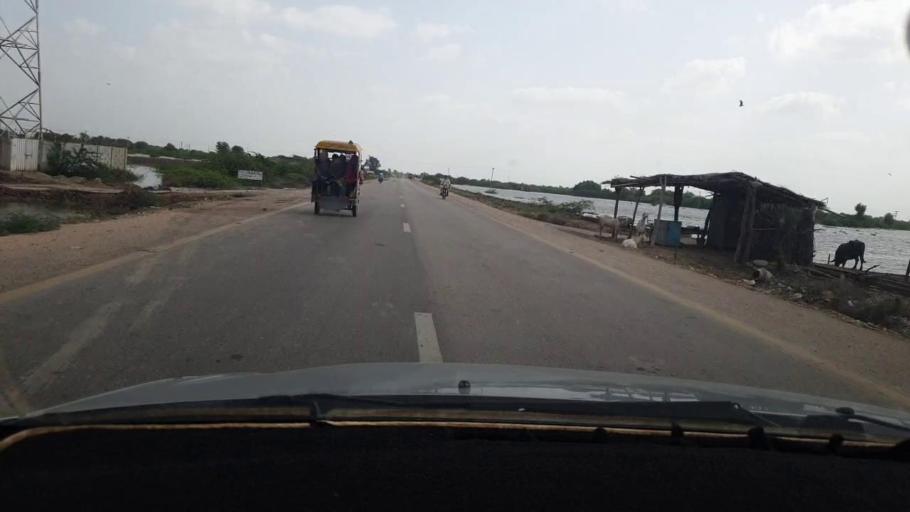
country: PK
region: Sindh
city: Naukot
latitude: 24.9909
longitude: 69.2916
